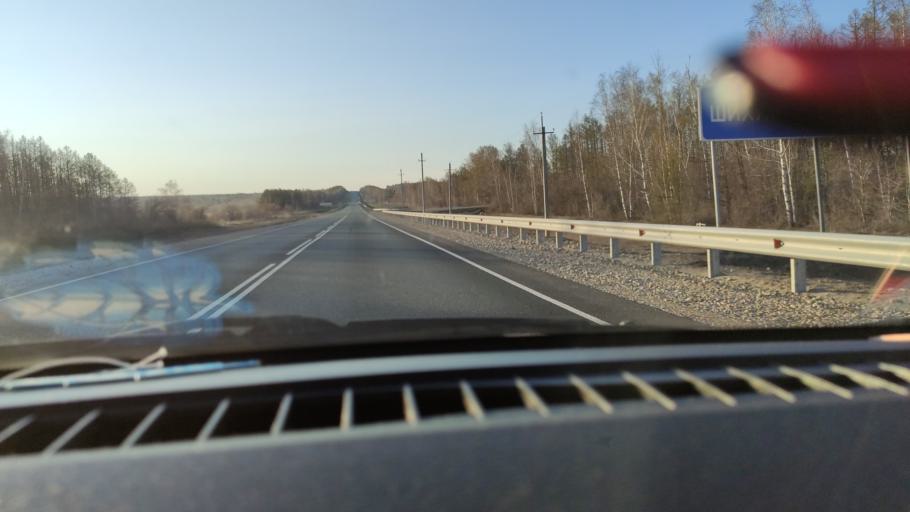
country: RU
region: Saratov
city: Shikhany
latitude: 52.1569
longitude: 47.1766
